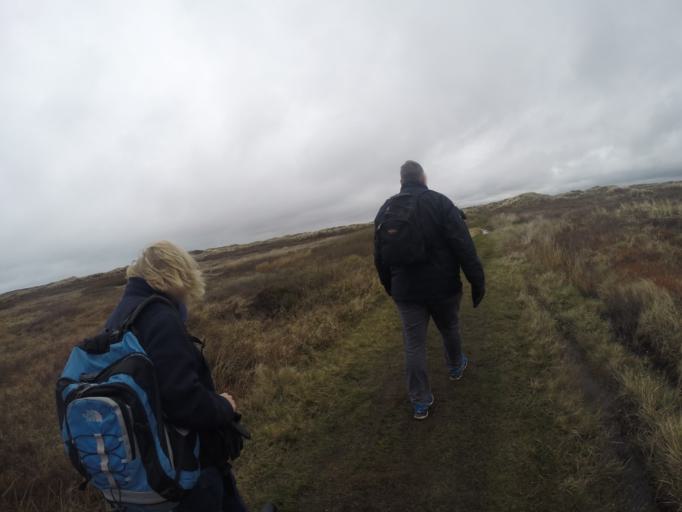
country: DK
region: Central Jutland
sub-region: Lemvig Kommune
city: Thyboron
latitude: 56.8286
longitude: 8.2644
